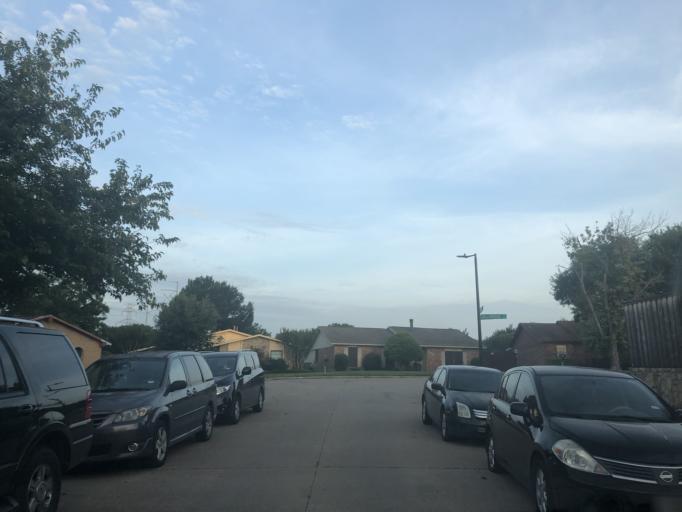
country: US
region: Texas
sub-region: Dallas County
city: Sunnyvale
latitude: 32.8347
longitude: -96.5937
